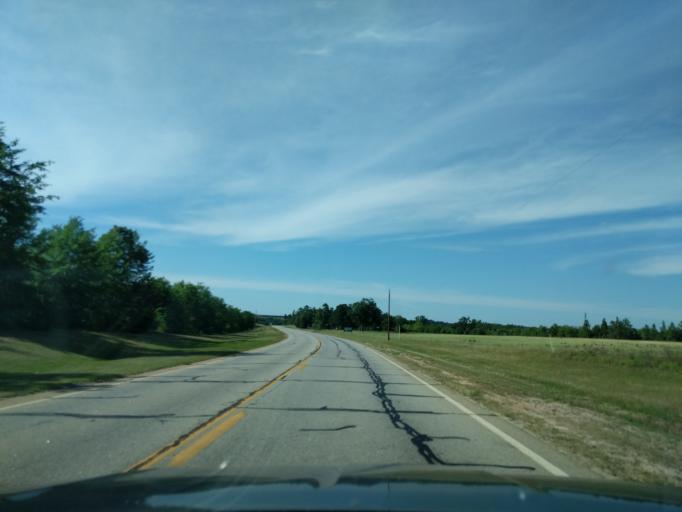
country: US
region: Georgia
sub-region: Jefferson County
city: Wrens
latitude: 33.2630
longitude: -82.3845
